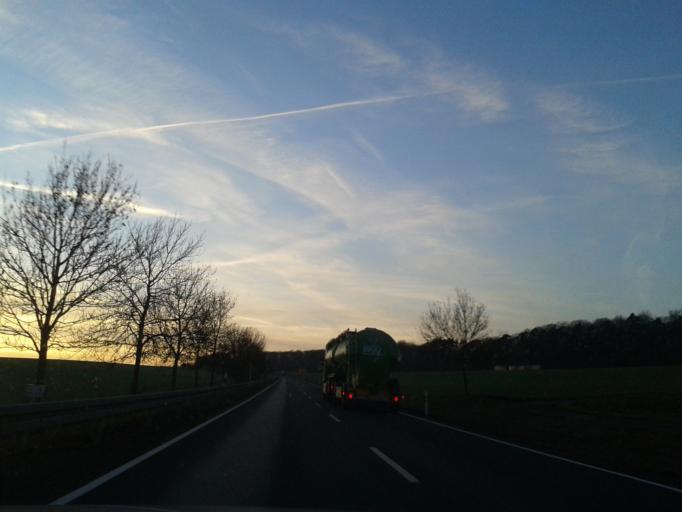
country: DE
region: Bavaria
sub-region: Regierungsbezirk Unterfranken
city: Aidhausen
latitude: 50.1151
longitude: 10.4441
